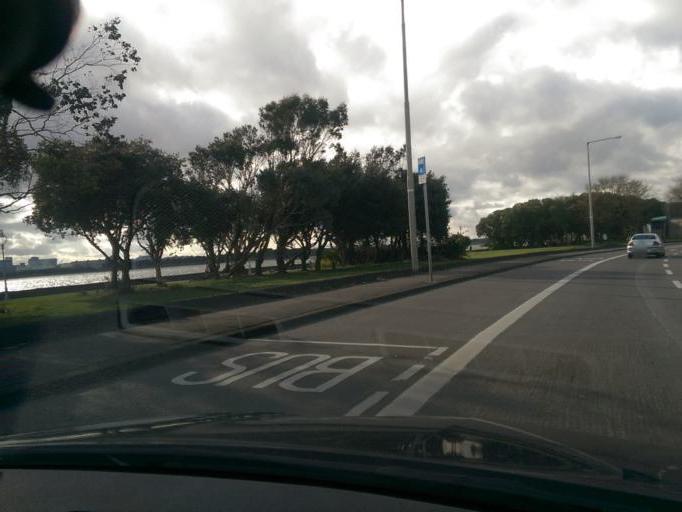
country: IE
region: Leinster
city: Dollymount
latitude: 53.3583
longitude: -6.1941
